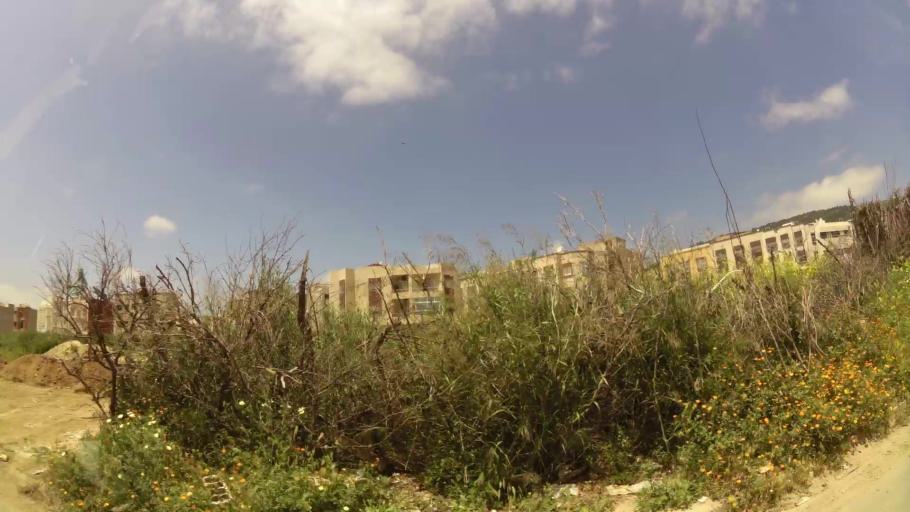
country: MA
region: Fes-Boulemane
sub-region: Fes
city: Fes
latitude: 34.0560
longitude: -5.0423
